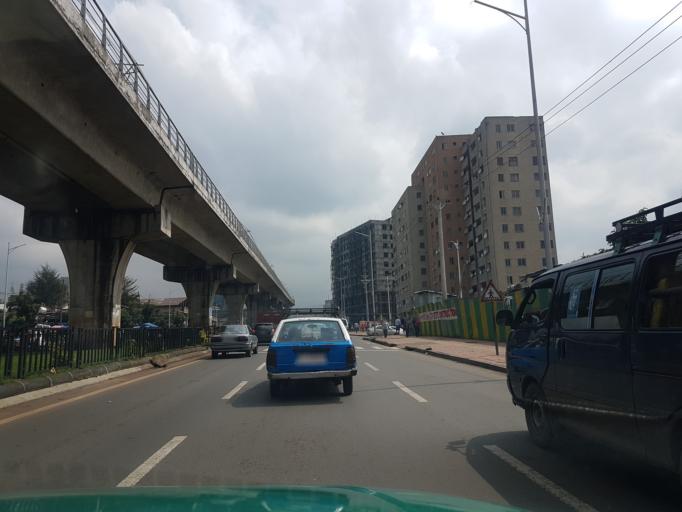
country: ET
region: Adis Abeba
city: Addis Ababa
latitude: 9.0160
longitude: 38.7349
